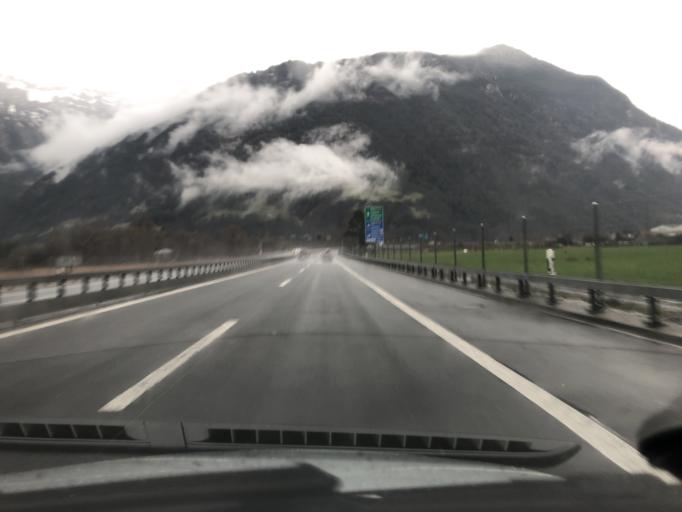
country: CH
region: Uri
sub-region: Uri
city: Seedorf
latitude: 46.8893
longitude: 8.6091
